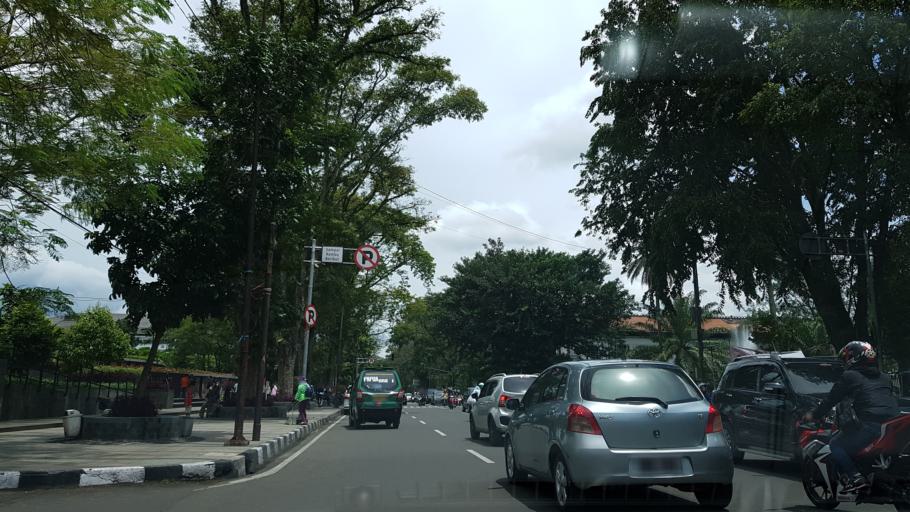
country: ID
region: West Java
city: Bandung
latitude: -6.9014
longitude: 107.6180
